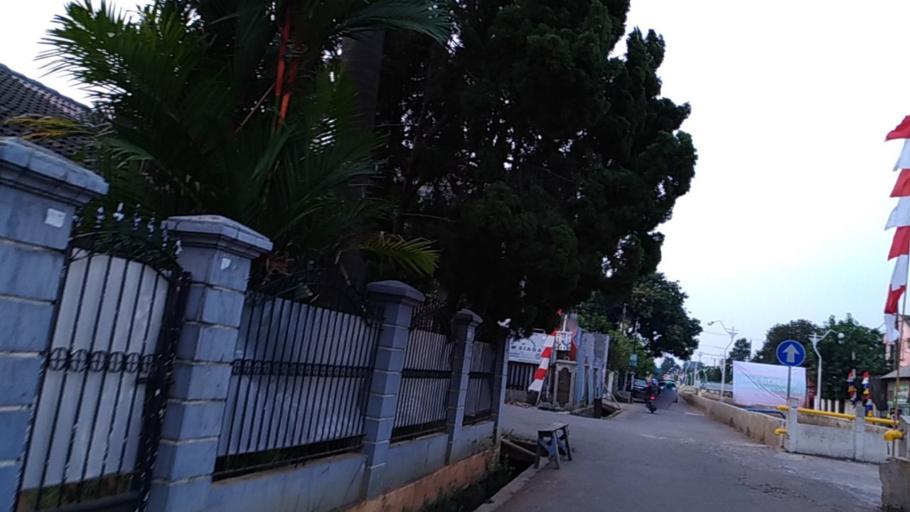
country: ID
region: West Java
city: Depok
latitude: -6.3758
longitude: 106.8583
